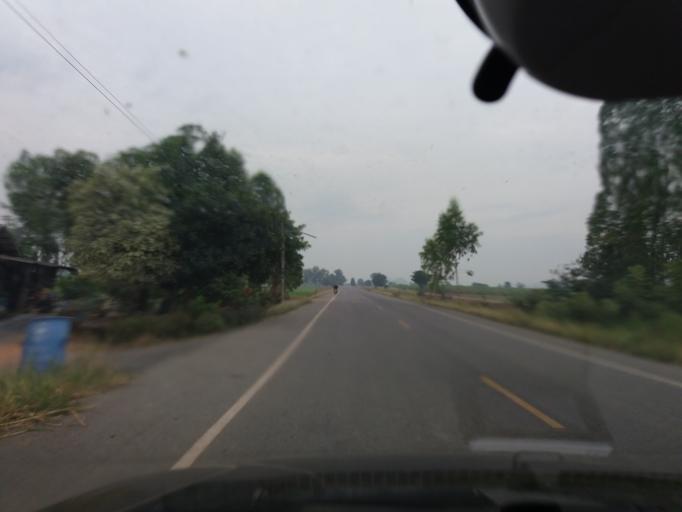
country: TH
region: Suphan Buri
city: Doem Bang Nang Buat
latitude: 14.8698
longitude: 100.1324
